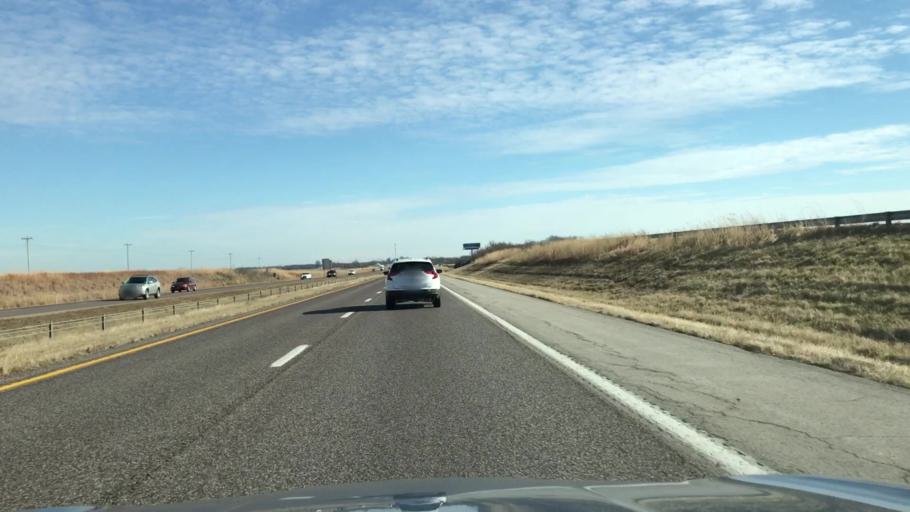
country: US
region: Missouri
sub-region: Callaway County
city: Fulton
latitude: 38.9519
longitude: -91.9864
